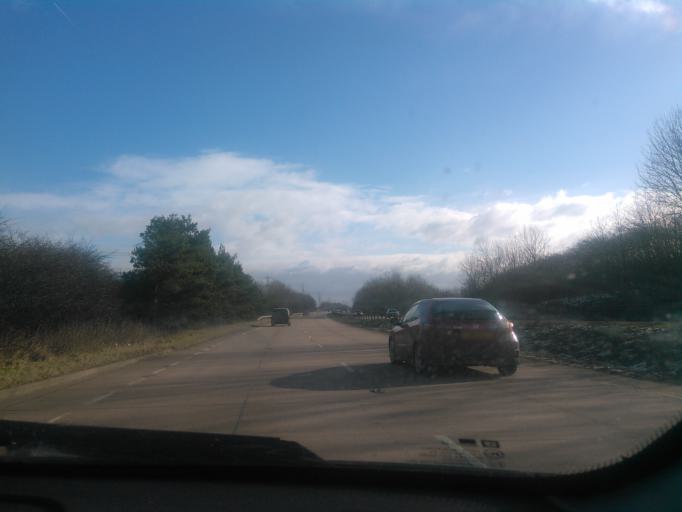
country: GB
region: England
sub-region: Staffordshire
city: Cheadle
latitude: 52.9319
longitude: -1.9563
